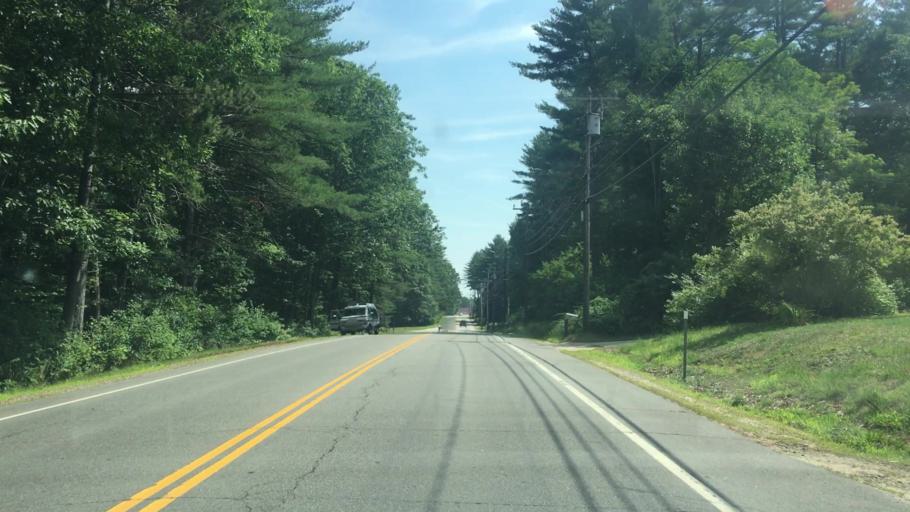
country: US
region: New Hampshire
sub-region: Strafford County
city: Rochester
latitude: 43.3637
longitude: -70.9803
